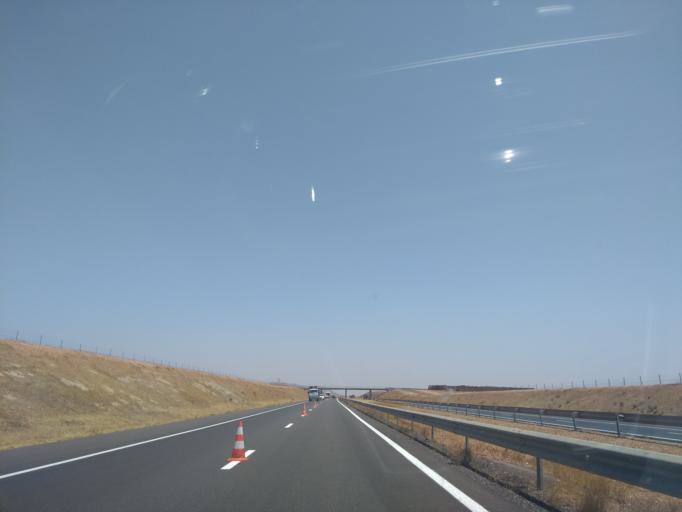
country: MA
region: Marrakech-Tensift-Al Haouz
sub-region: Kelaa-Des-Sraghna
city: Sidi Abdallah
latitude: 32.4340
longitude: -7.9315
